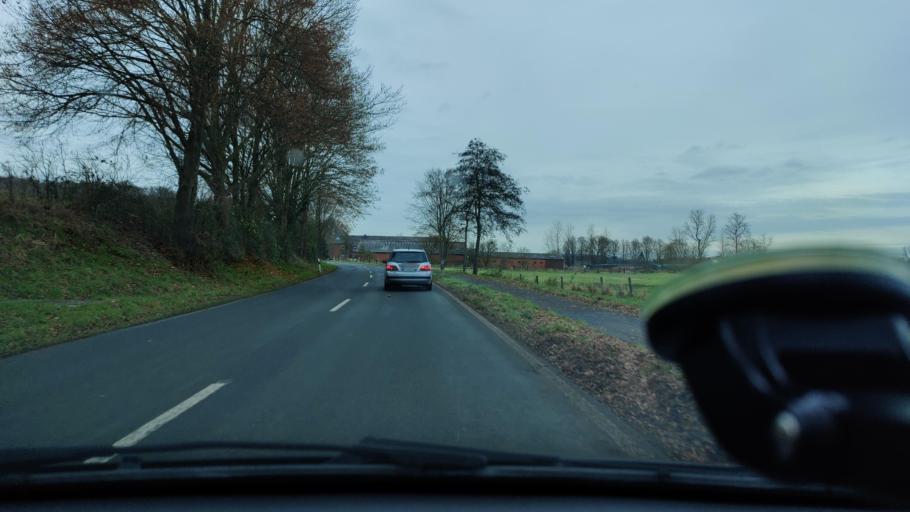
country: DE
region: North Rhine-Westphalia
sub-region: Regierungsbezirk Dusseldorf
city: Sonsbeck
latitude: 51.6283
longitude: 6.4143
